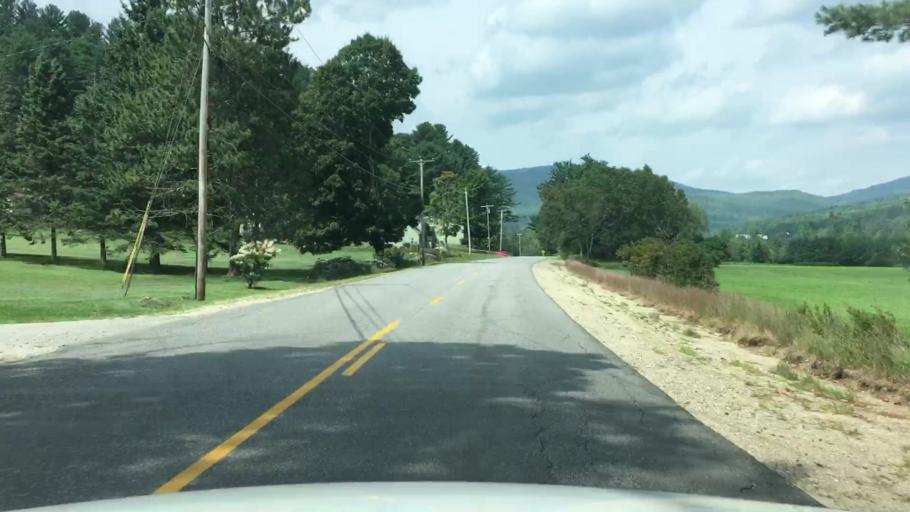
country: US
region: Maine
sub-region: Oxford County
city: Rumford
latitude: 44.5312
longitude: -70.6419
